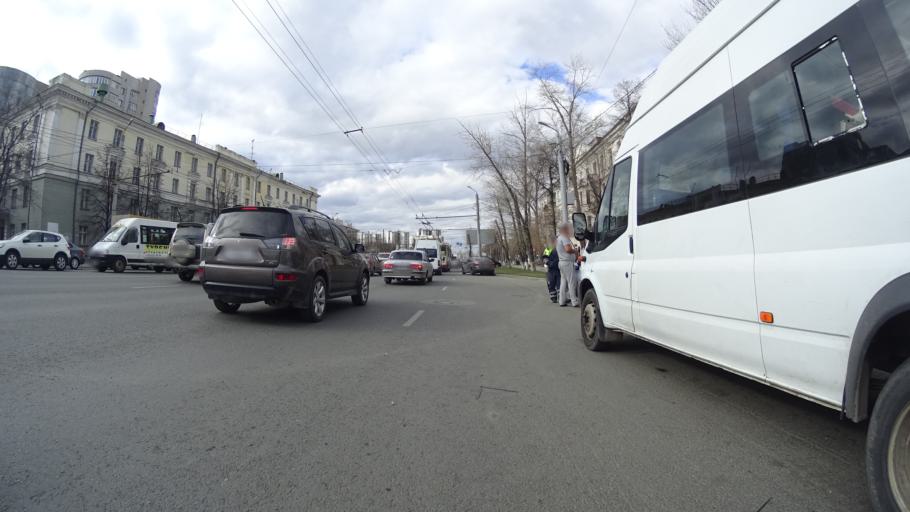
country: RU
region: Chelyabinsk
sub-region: Gorod Chelyabinsk
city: Chelyabinsk
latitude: 55.1609
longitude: 61.3813
